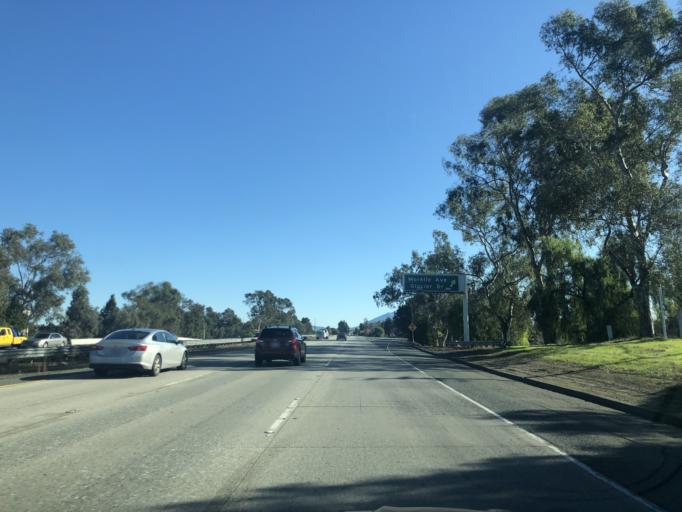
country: US
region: California
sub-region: Contra Costa County
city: Vine Hill
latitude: 37.9935
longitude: -122.1053
